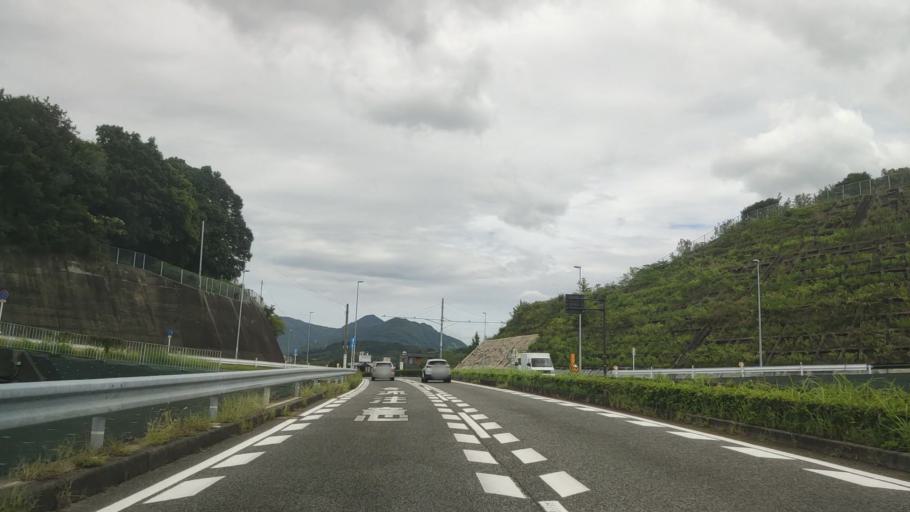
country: JP
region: Wakayama
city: Tanabe
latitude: 33.7328
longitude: 135.4006
